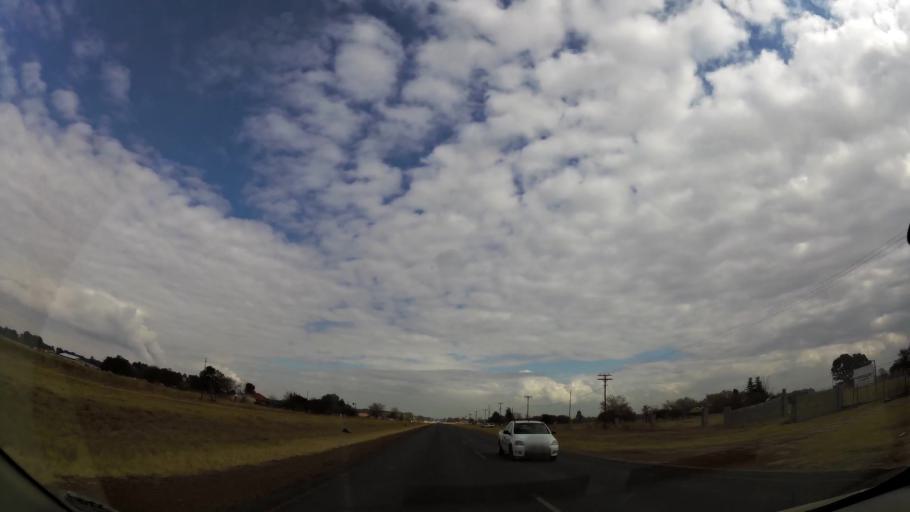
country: ZA
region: Gauteng
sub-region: Sedibeng District Municipality
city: Meyerton
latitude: -26.6367
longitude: 28.0567
